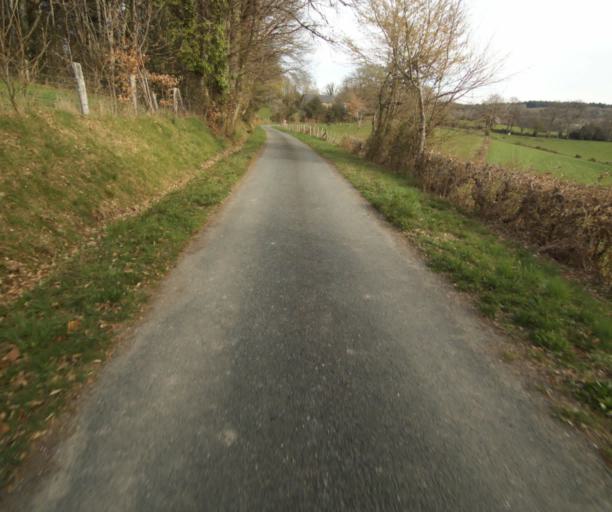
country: FR
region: Limousin
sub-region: Departement de la Correze
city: Chamboulive
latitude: 45.4399
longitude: 1.7878
